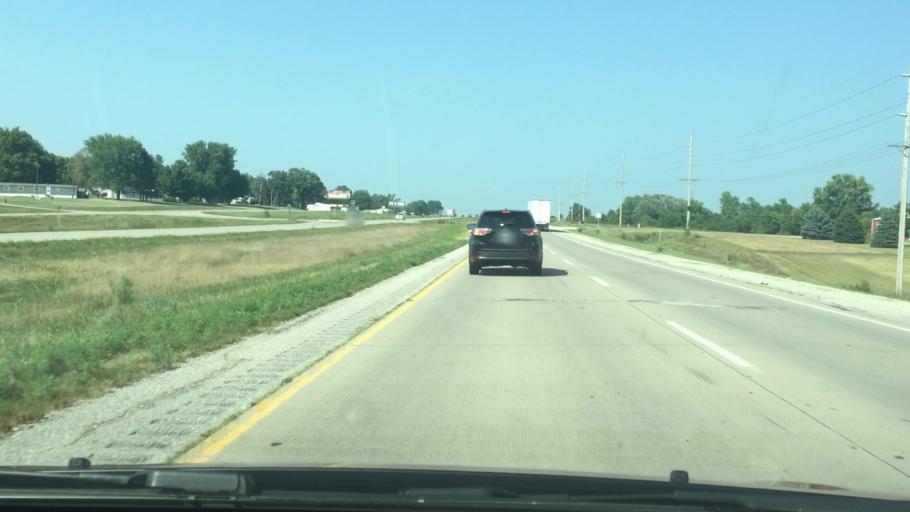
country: US
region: Iowa
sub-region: Muscatine County
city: Muscatine
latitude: 41.4695
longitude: -91.0026
